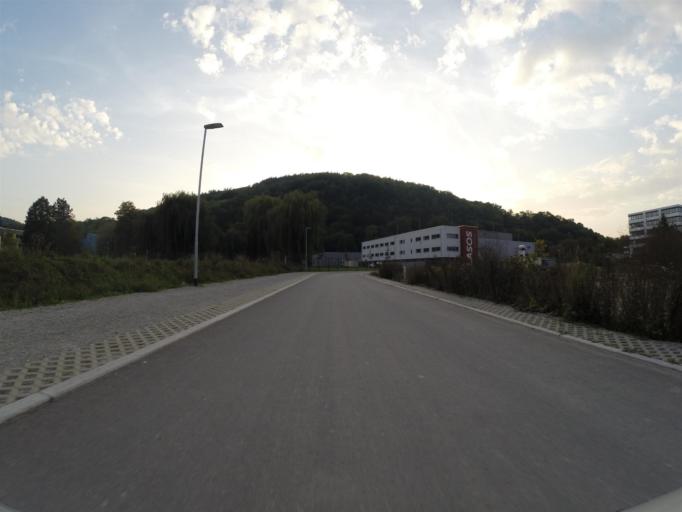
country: DE
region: Thuringia
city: Sulza
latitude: 50.8848
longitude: 11.5917
